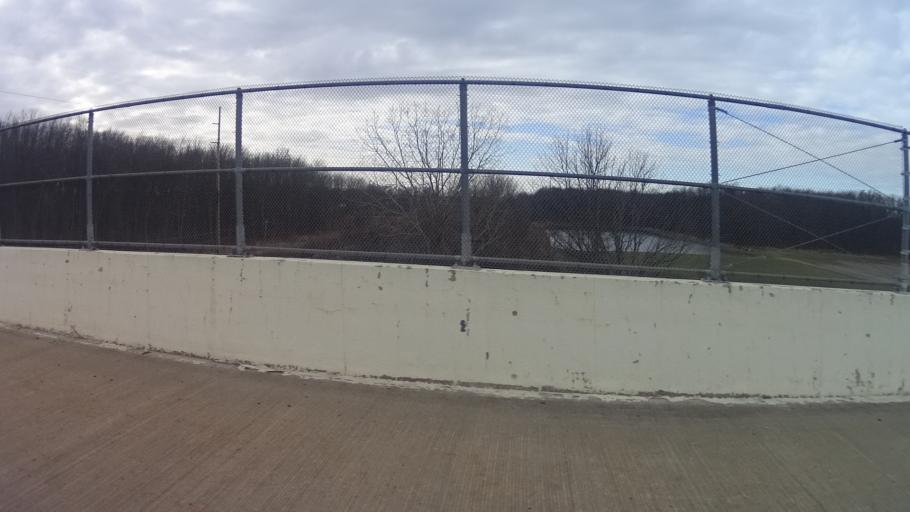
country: US
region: Ohio
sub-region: Lorain County
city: North Ridgeville
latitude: 41.3759
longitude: -82.0210
